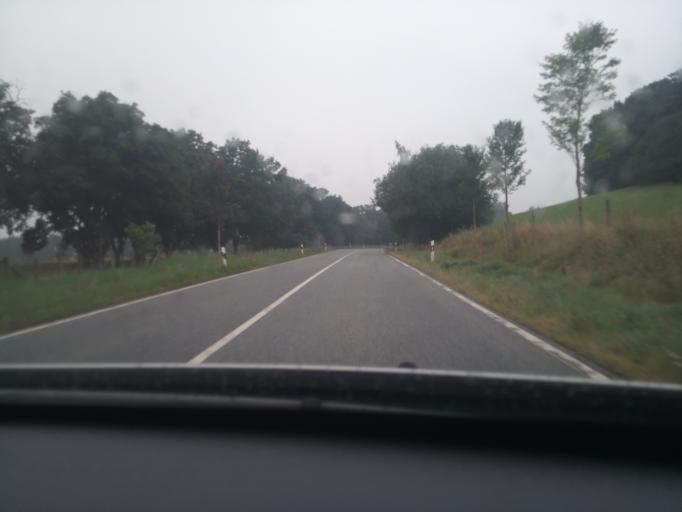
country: DE
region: Mecklenburg-Vorpommern
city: Strasburg
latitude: 53.4919
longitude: 13.6934
